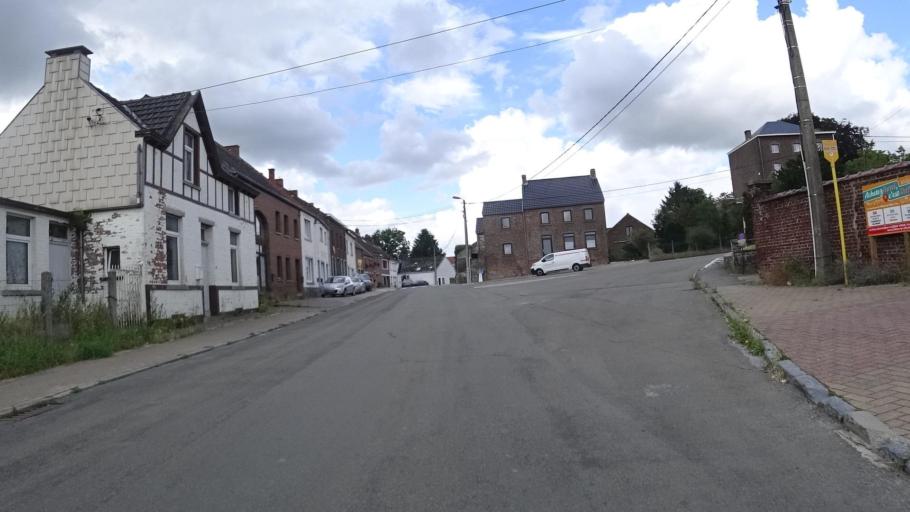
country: BE
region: Wallonia
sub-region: Province du Brabant Wallon
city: Villers-la-Ville
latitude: 50.5481
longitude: 4.5542
